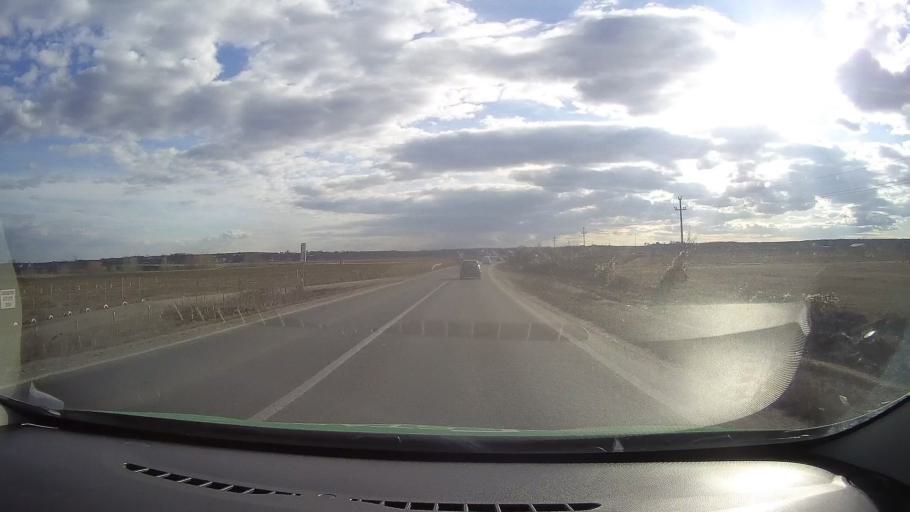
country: RO
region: Dambovita
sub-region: Comuna Lucieni
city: Lucieni
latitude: 44.8600
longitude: 25.4164
